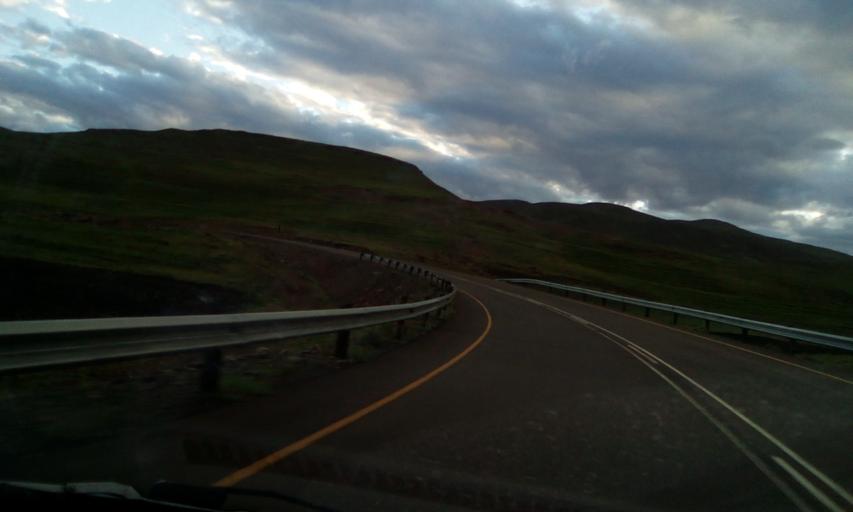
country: LS
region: Maseru
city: Nako
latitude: -29.8052
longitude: 28.0279
